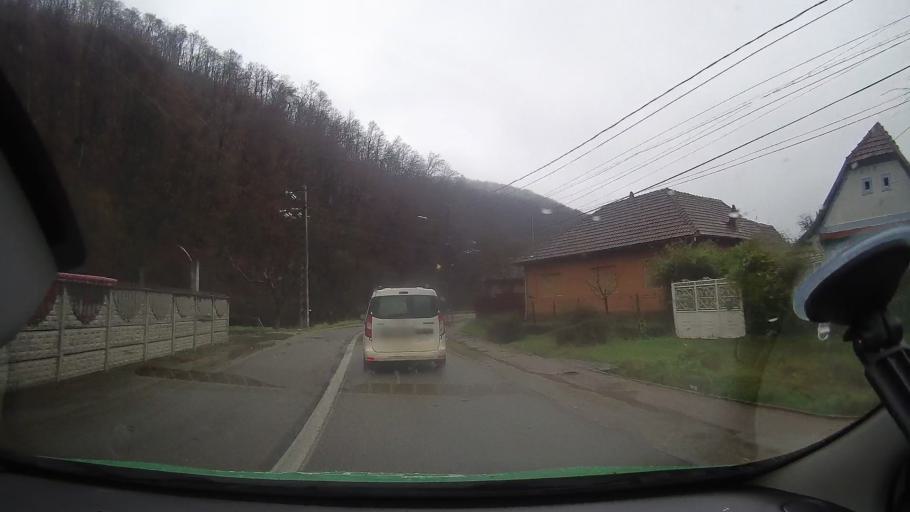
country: RO
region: Arad
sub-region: Comuna Moneasa
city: Moneasa
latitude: 46.4516
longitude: 22.2479
